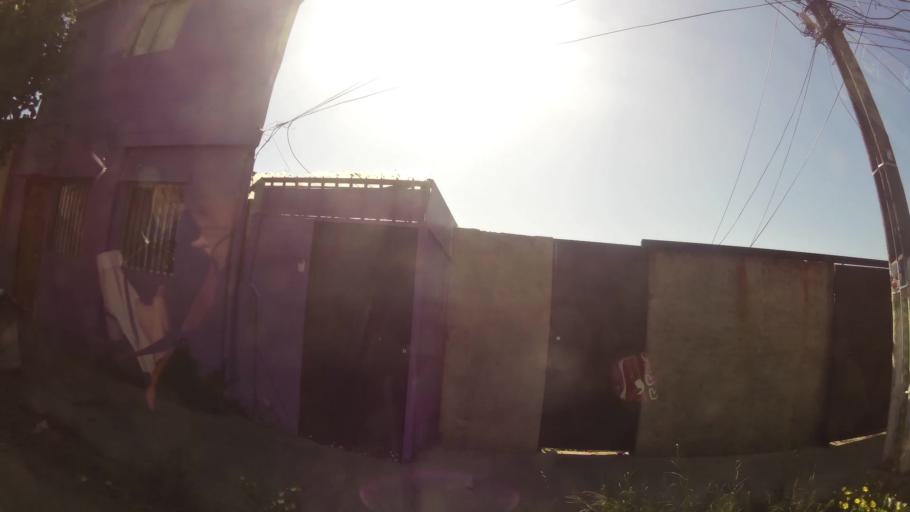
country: CL
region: Valparaiso
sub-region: Provincia de Valparaiso
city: Valparaiso
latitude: -33.0431
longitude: -71.6337
